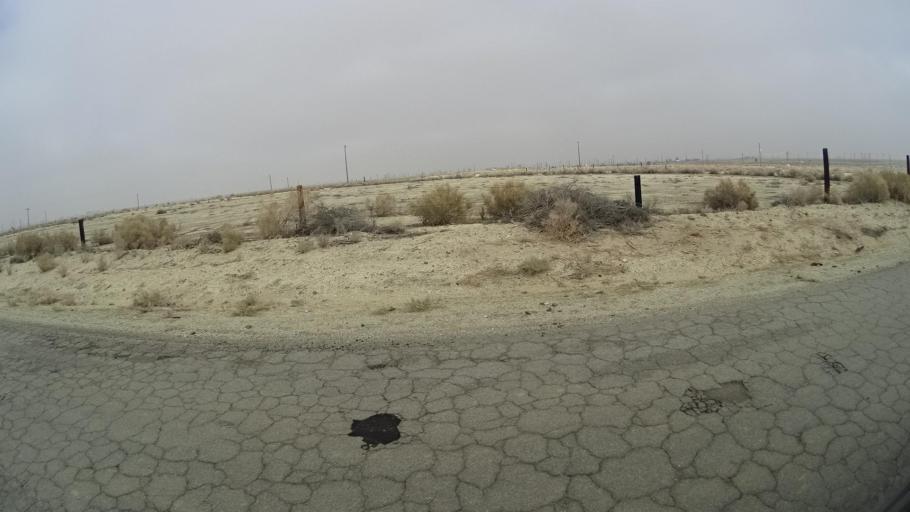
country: US
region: California
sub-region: Kern County
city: Maricopa
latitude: 35.0388
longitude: -119.3811
